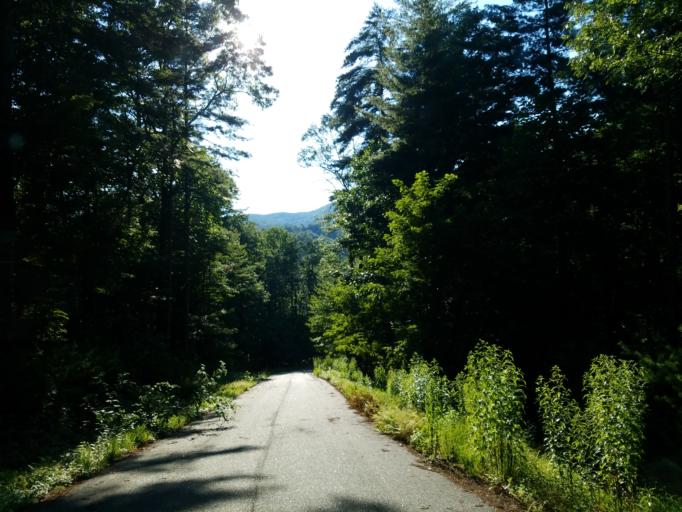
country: US
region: Georgia
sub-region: Union County
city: Blairsville
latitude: 34.7587
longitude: -84.1035
